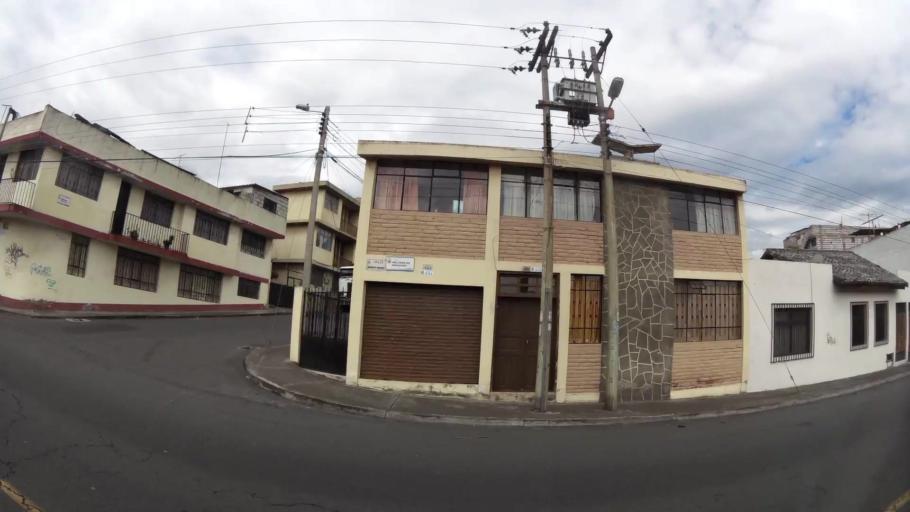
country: EC
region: Cotopaxi
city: Latacunga
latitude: -0.9281
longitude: -78.6230
